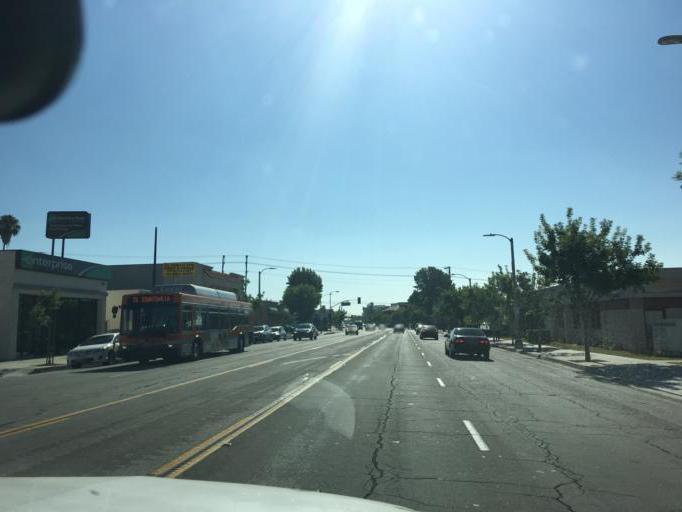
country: US
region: California
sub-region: Los Angeles County
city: San Gabriel
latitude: 34.1024
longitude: -118.1043
